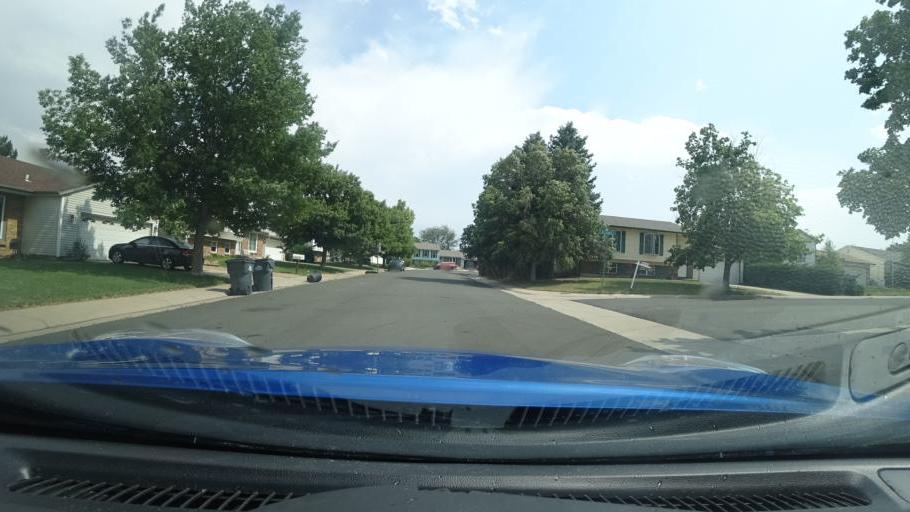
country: US
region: Colorado
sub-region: Adams County
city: Aurora
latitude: 39.6944
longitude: -104.7643
